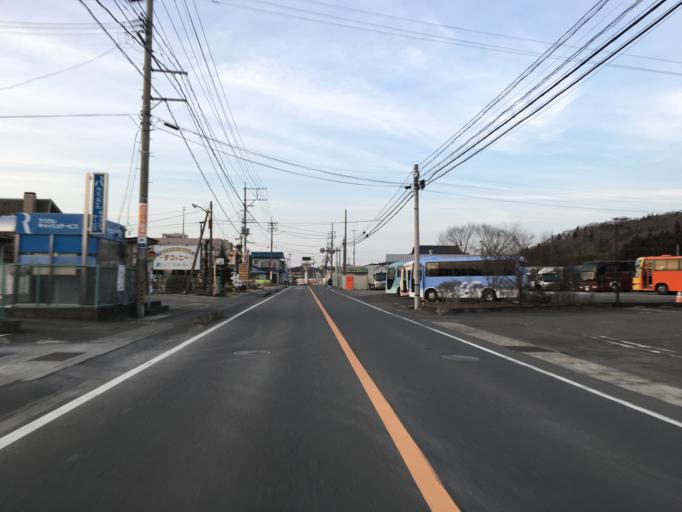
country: JP
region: Fukushima
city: Ishikawa
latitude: 37.0163
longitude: 140.3916
